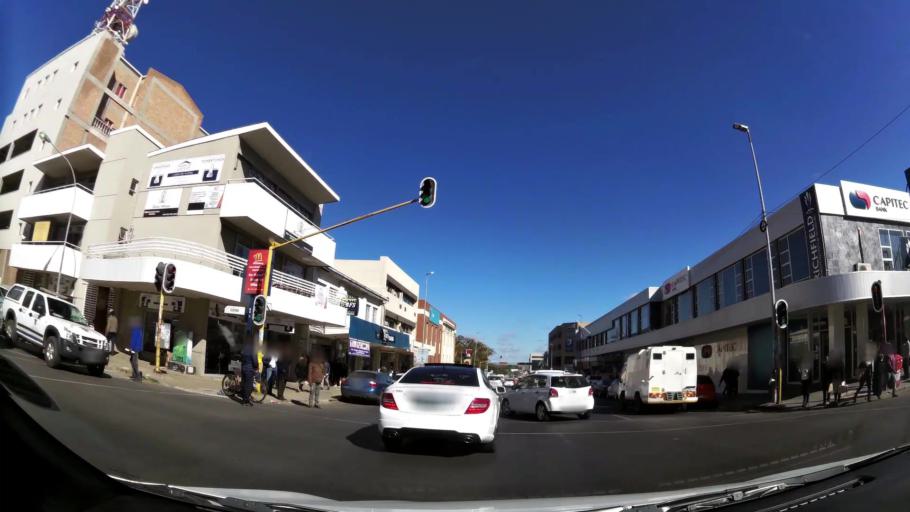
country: ZA
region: Limpopo
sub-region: Capricorn District Municipality
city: Polokwane
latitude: -23.9112
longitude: 29.4541
